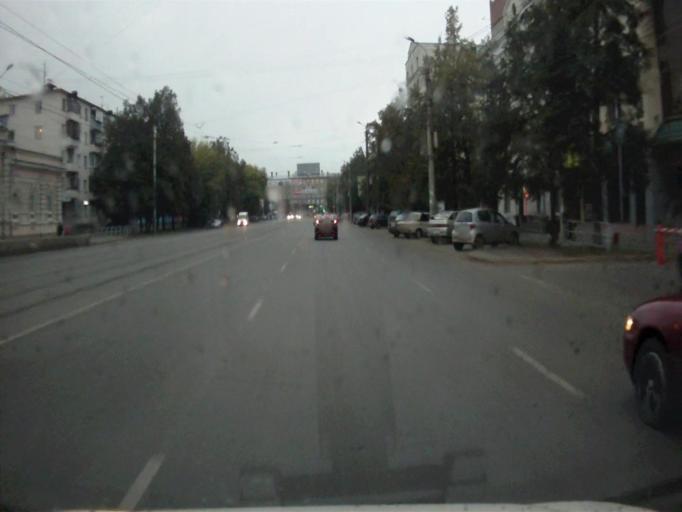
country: RU
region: Chelyabinsk
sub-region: Gorod Chelyabinsk
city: Chelyabinsk
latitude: 55.1800
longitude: 61.3994
